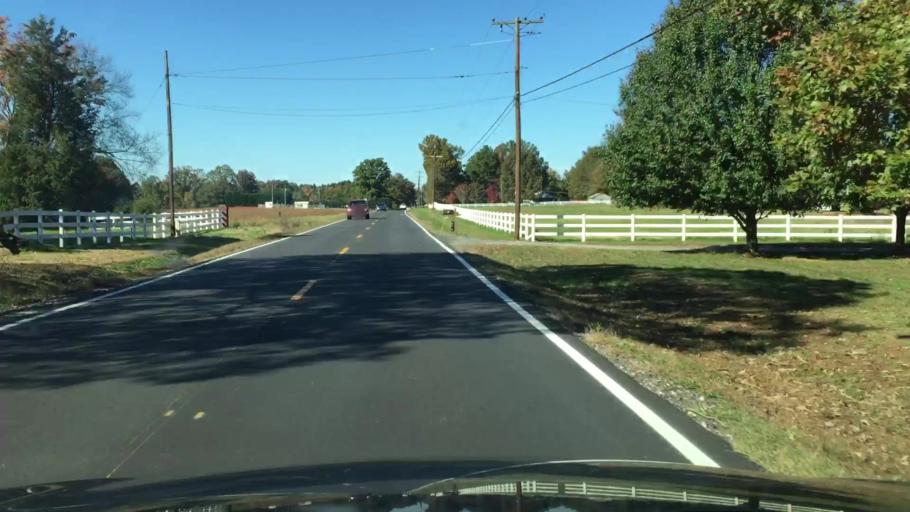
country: US
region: North Carolina
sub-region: Iredell County
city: Mooresville
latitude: 35.5730
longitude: -80.7787
